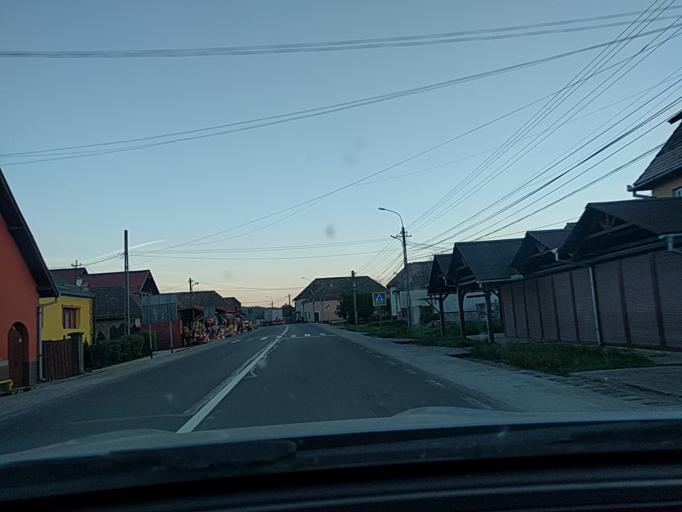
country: RO
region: Mures
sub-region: Comuna Balauseri
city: Chendu
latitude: 46.3868
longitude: 24.7294
